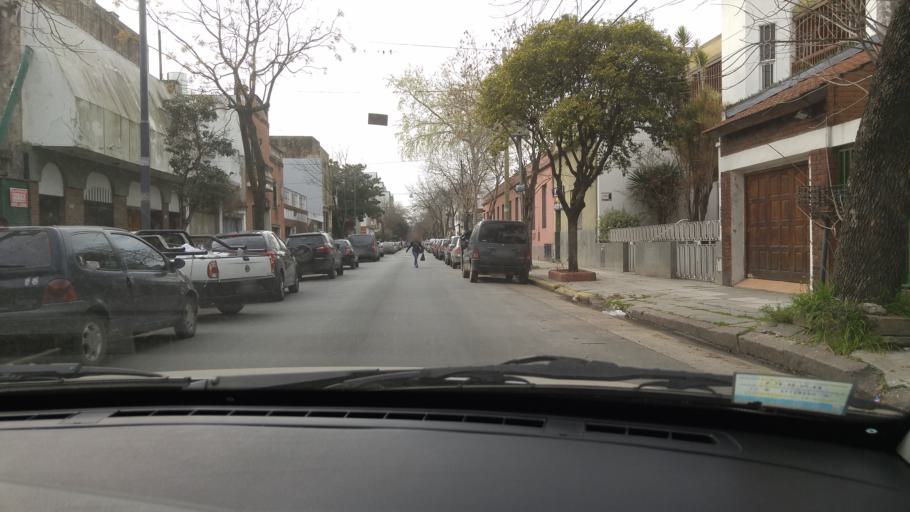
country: AR
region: Buenos Aires F.D.
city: Villa Santa Rita
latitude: -34.6266
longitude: -58.4816
